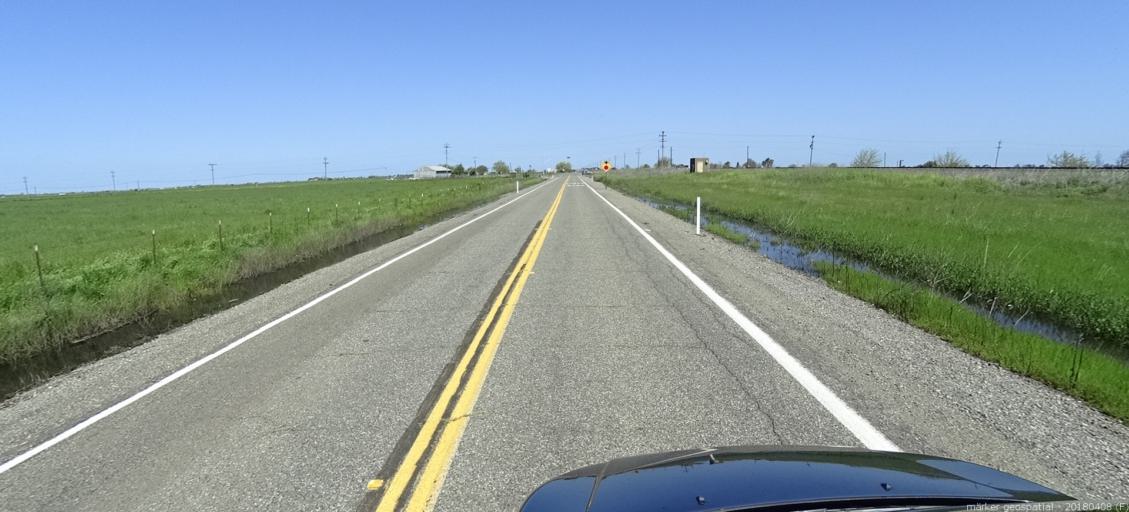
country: US
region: California
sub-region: San Joaquin County
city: Thornton
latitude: 38.2880
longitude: -121.4411
